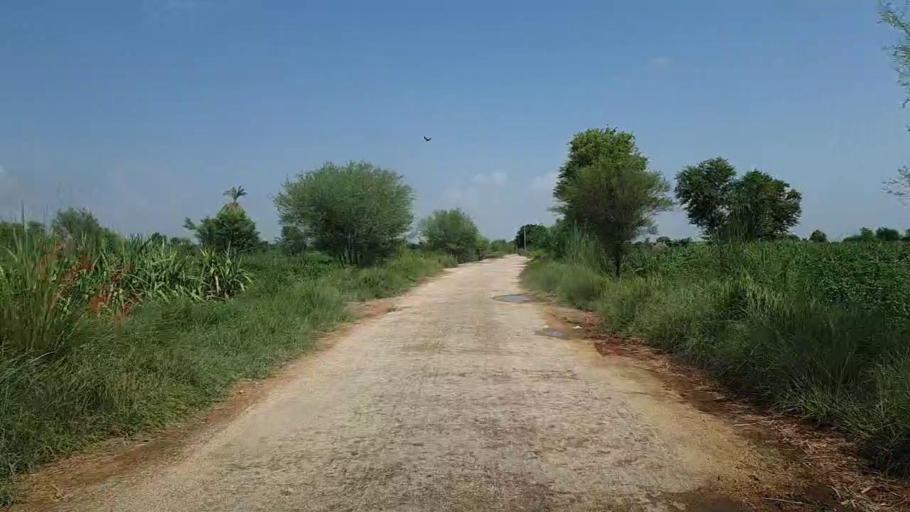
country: PK
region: Sindh
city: Bhiria
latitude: 26.8768
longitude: 68.2467
